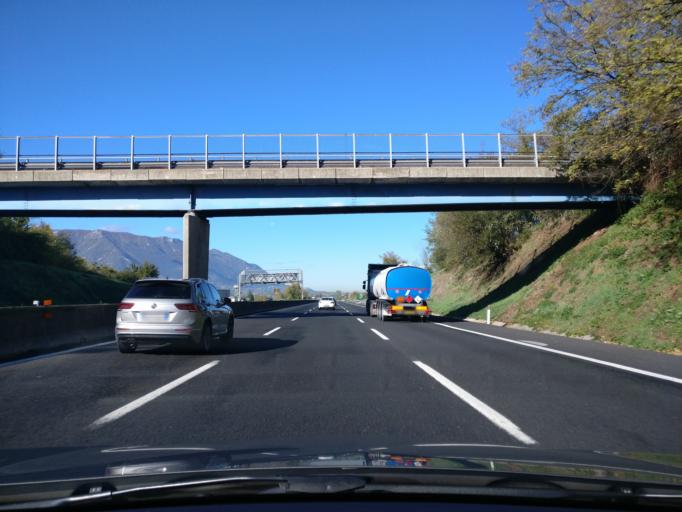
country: IT
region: Latium
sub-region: Provincia di Frosinone
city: Frosinone
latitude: 41.6263
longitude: 13.2937
